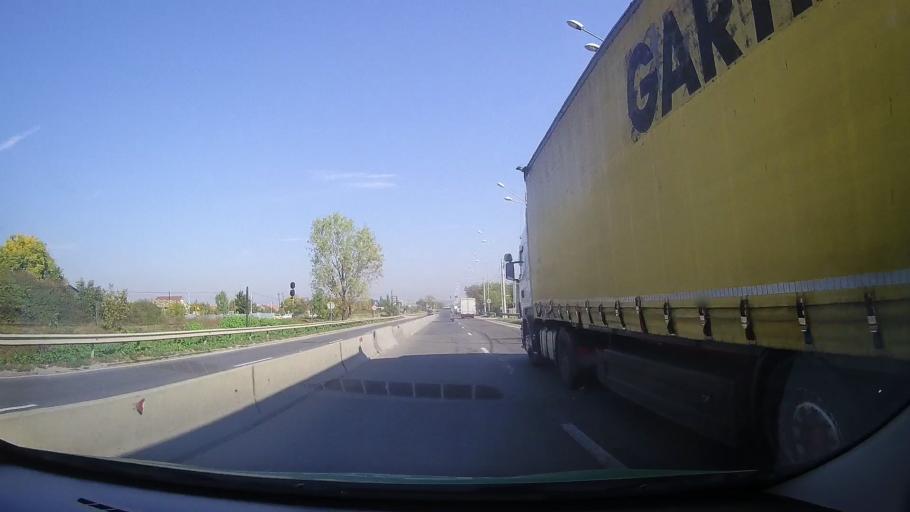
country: RO
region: Bihor
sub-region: Comuna Santandrei
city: Santandrei
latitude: 47.0530
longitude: 21.8881
